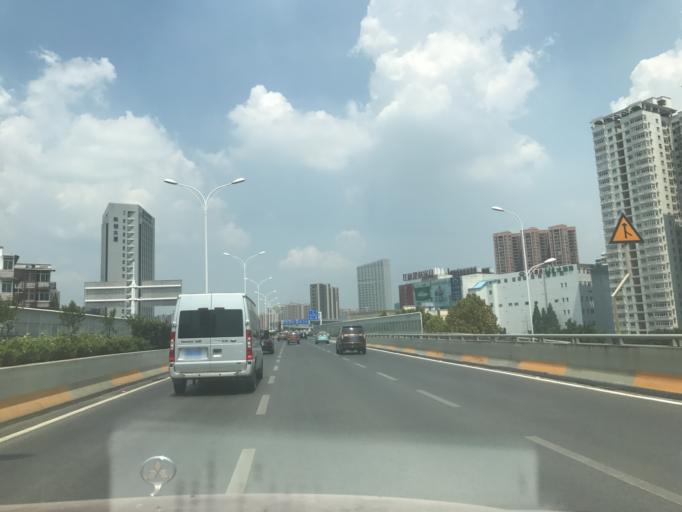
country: CN
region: Hubei
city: Jiang'an
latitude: 30.6246
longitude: 114.2870
